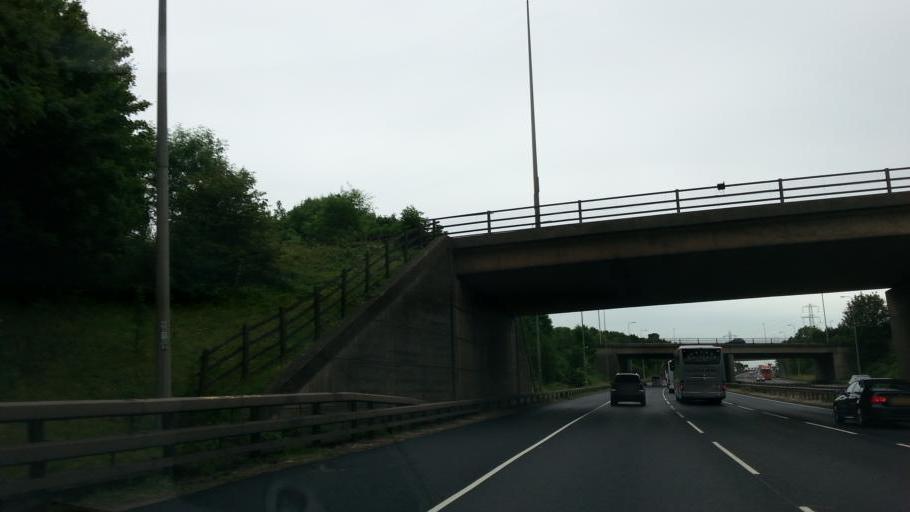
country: GB
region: England
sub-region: Solihull
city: Bickenhill
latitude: 52.4465
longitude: -1.7091
